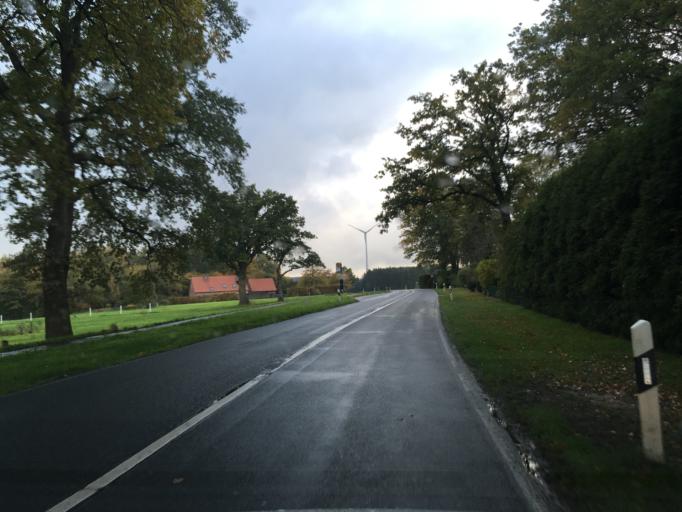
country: DE
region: North Rhine-Westphalia
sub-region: Regierungsbezirk Munster
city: Klein Reken
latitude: 51.8318
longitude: 7.0213
